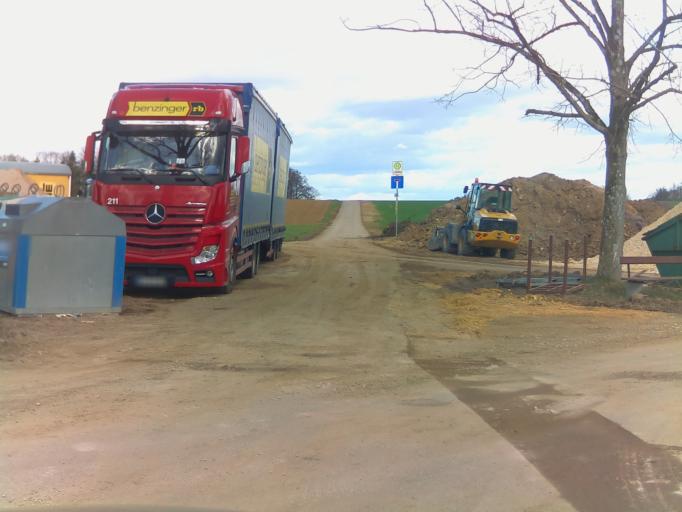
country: DE
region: Baden-Wuerttemberg
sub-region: Regierungsbezirk Stuttgart
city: Welzheim
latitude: 48.8726
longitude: 9.5897
